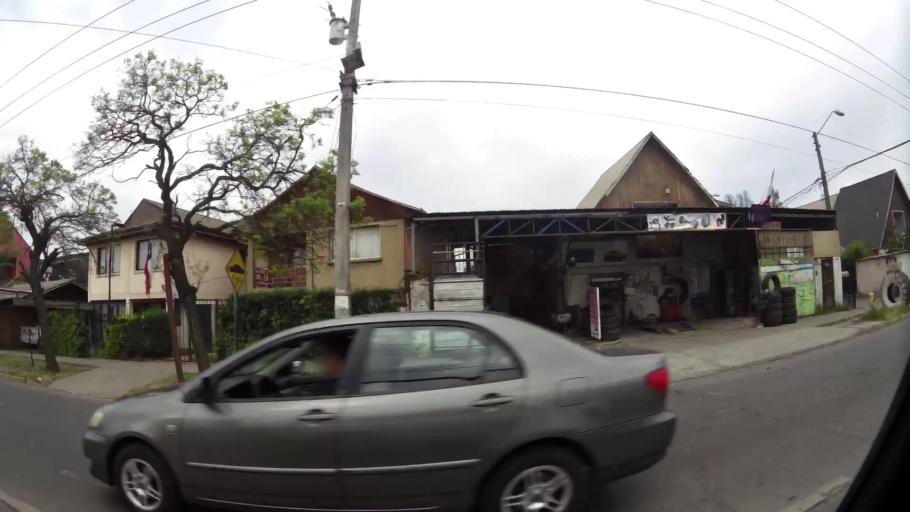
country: CL
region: Santiago Metropolitan
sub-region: Provincia de Santiago
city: Lo Prado
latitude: -33.4999
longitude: -70.7450
